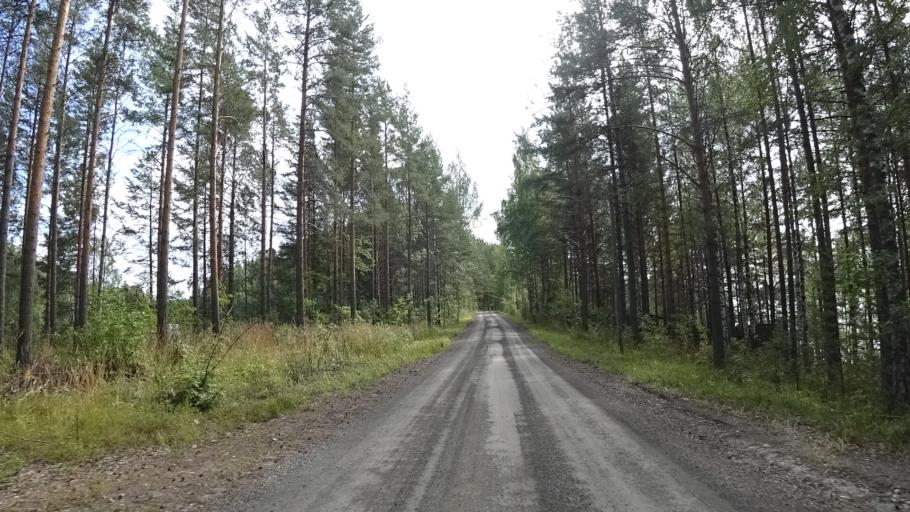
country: FI
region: North Karelia
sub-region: Joensuu
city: Pyhaeselkae
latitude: 62.3786
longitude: 29.8097
